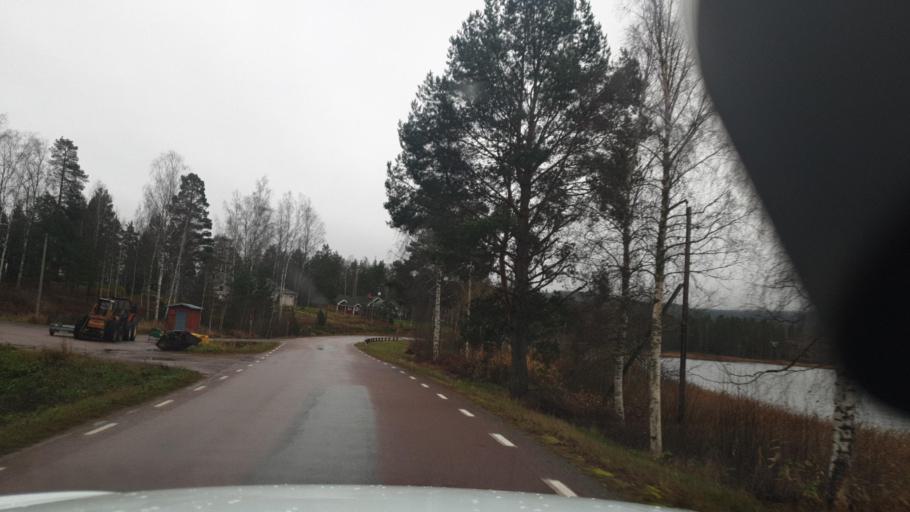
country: SE
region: Vaermland
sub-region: Arvika Kommun
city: Arvika
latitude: 59.5268
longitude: 12.8262
